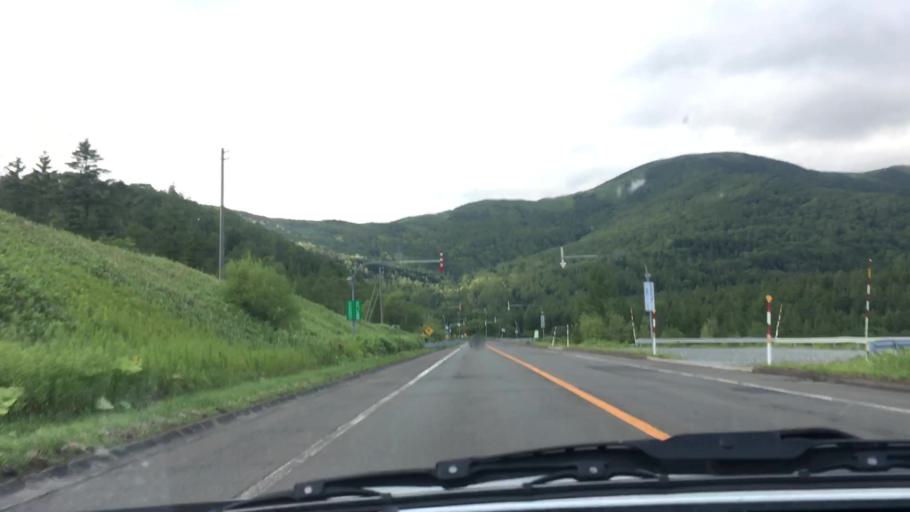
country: JP
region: Hokkaido
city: Shimo-furano
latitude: 43.1353
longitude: 142.7552
